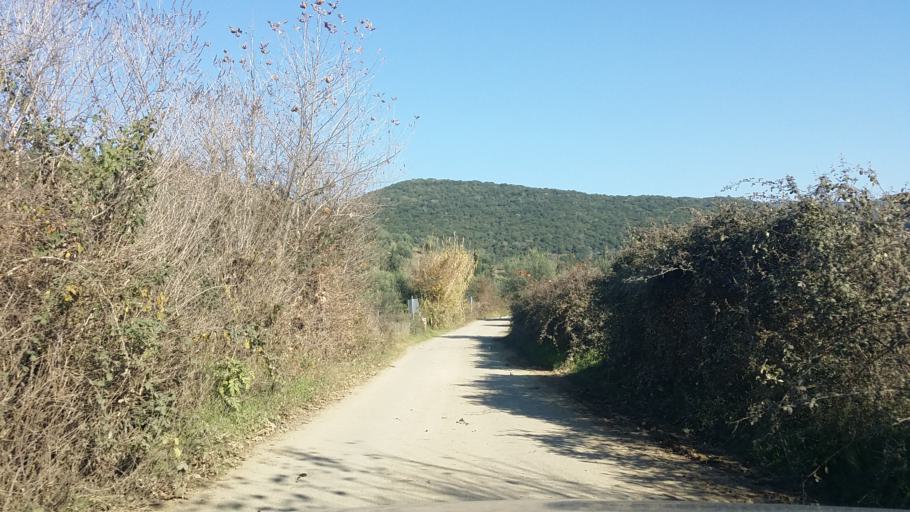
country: GR
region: West Greece
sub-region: Nomos Aitolias kai Akarnanias
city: Krikellos
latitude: 38.9585
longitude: 21.1873
